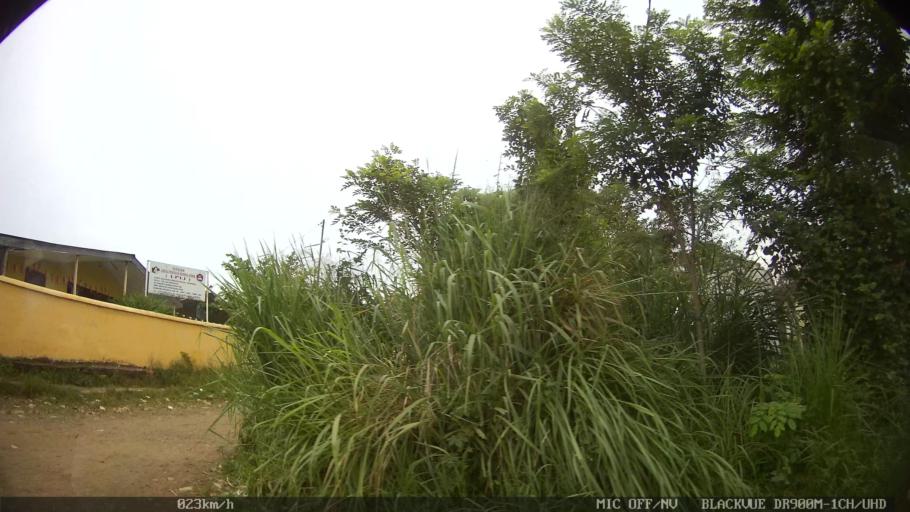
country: ID
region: North Sumatra
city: Deli Tua
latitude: 3.5430
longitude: 98.7336
